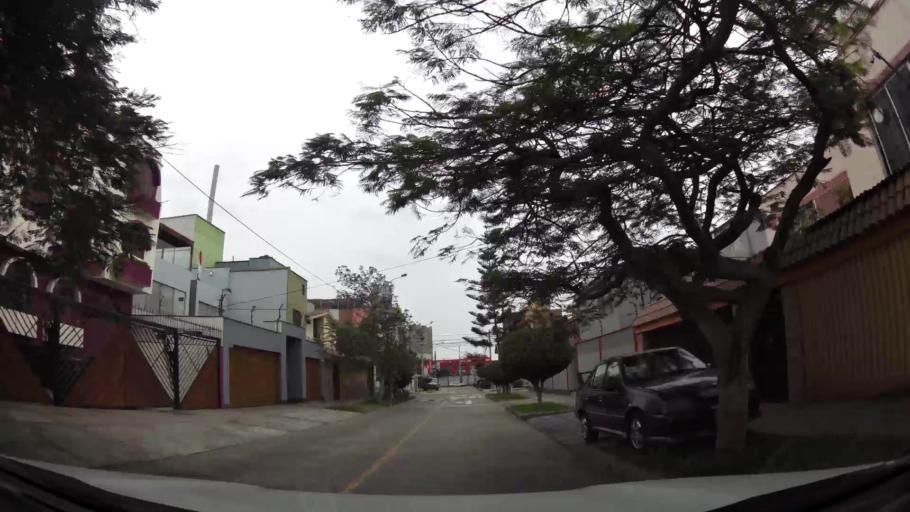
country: PE
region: Lima
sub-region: Lima
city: San Luis
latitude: -12.1048
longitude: -77.0051
